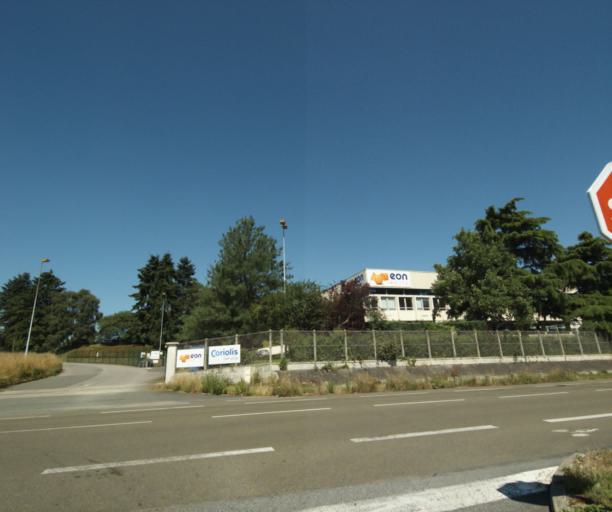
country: FR
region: Pays de la Loire
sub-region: Departement de la Mayenne
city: Laval
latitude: 48.0721
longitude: -0.7454
